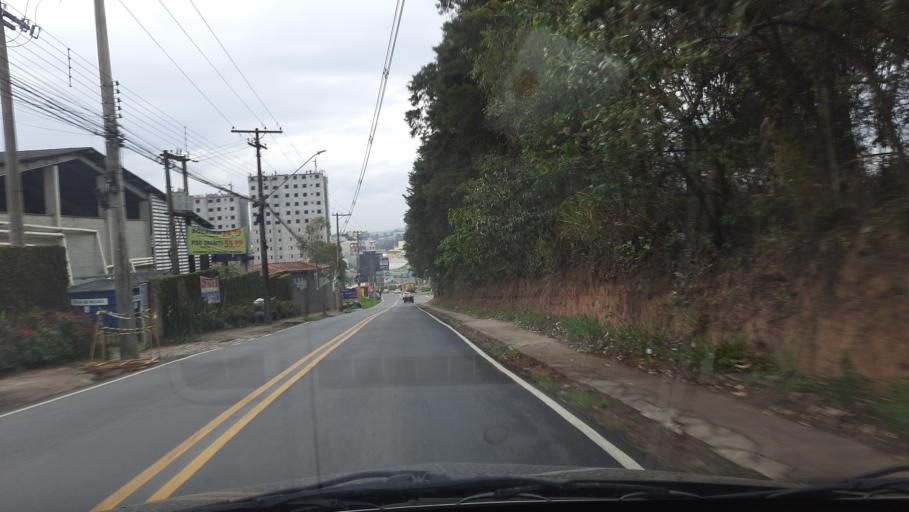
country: BR
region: Sao Paulo
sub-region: Caieiras
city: Caieiras
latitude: -23.3827
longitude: -46.7114
